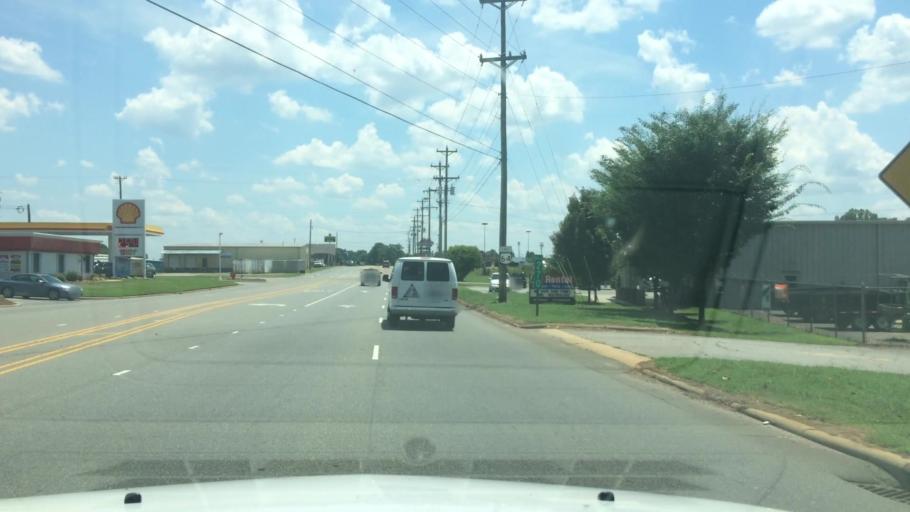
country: US
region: North Carolina
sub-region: Iredell County
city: Statesville
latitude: 35.7996
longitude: -80.9405
